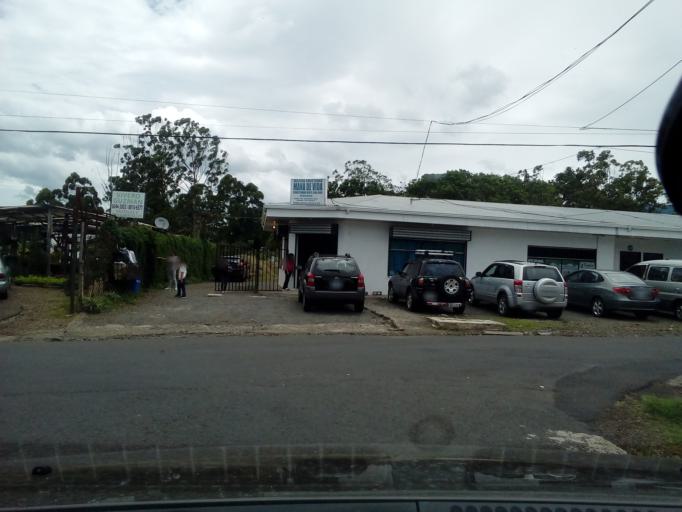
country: CR
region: Heredia
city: San Josecito
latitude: 10.0163
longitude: -84.1086
